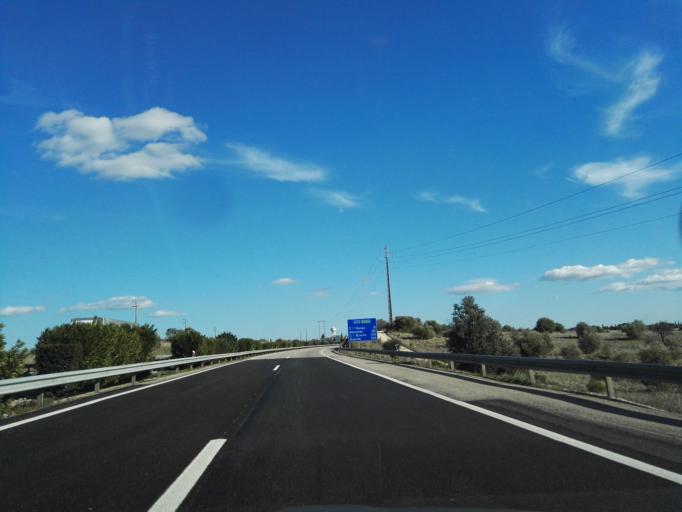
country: PT
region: Santarem
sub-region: Alcanena
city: Alcanena
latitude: 39.4790
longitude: -8.6145
